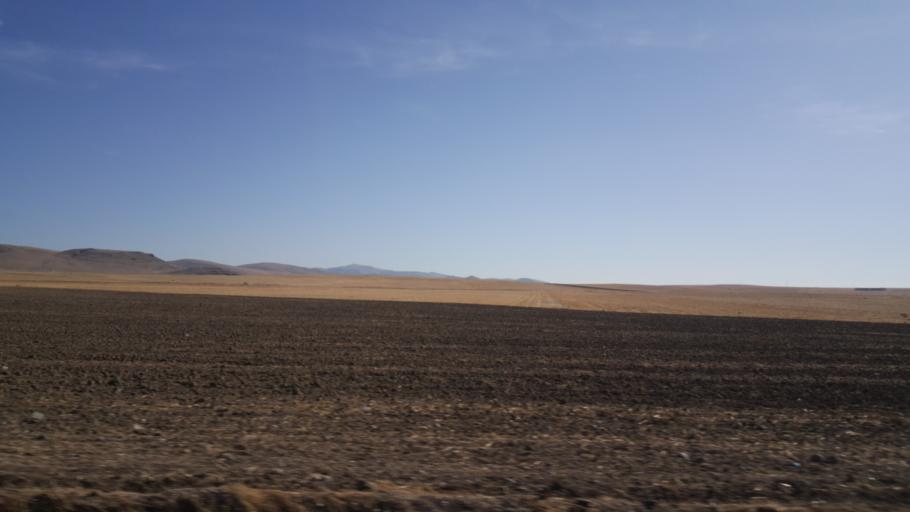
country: TR
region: Ankara
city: Yenice
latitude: 39.3467
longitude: 32.7621
